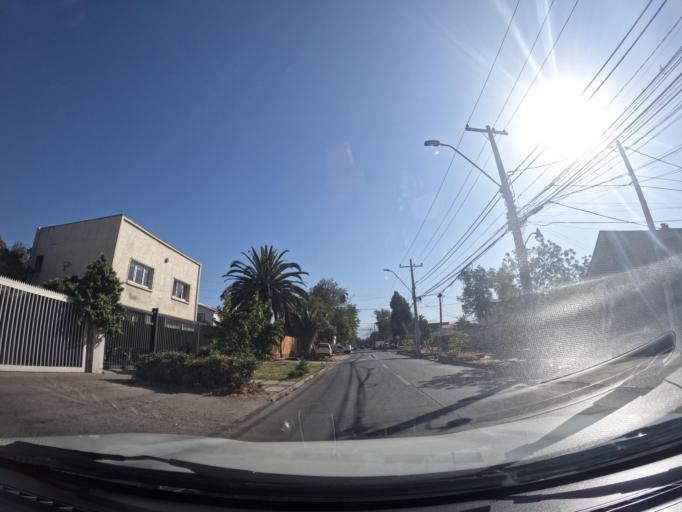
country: CL
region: Santiago Metropolitan
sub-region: Provincia de Santiago
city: Villa Presidente Frei, Nunoa, Santiago, Chile
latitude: -33.4624
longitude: -70.5678
